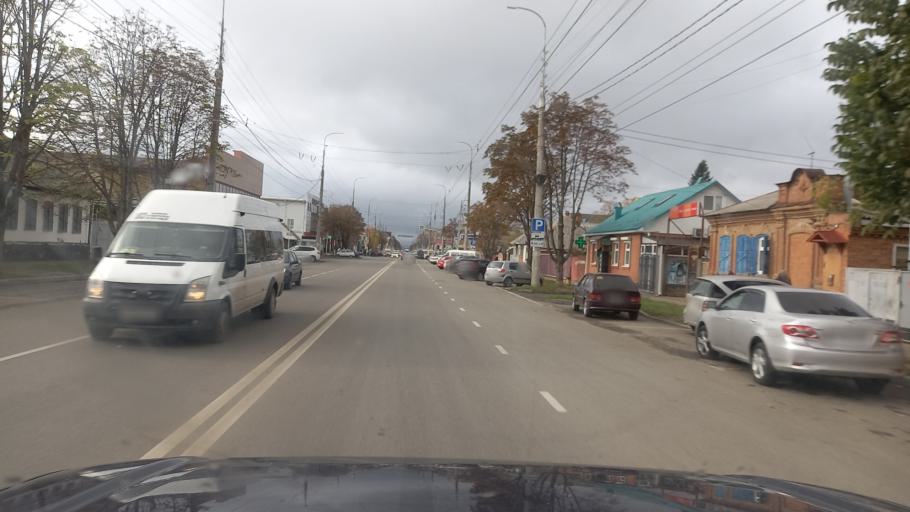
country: RU
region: Adygeya
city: Maykop
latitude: 44.6083
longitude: 40.1140
